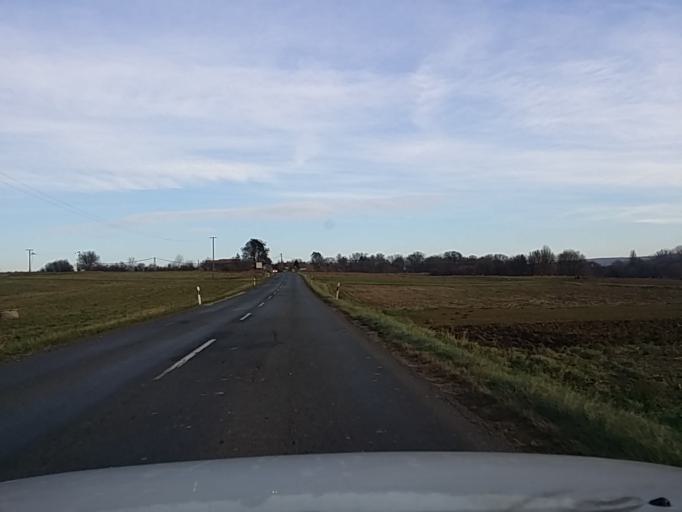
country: HU
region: Veszprem
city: Urkut
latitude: 46.9901
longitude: 17.6904
